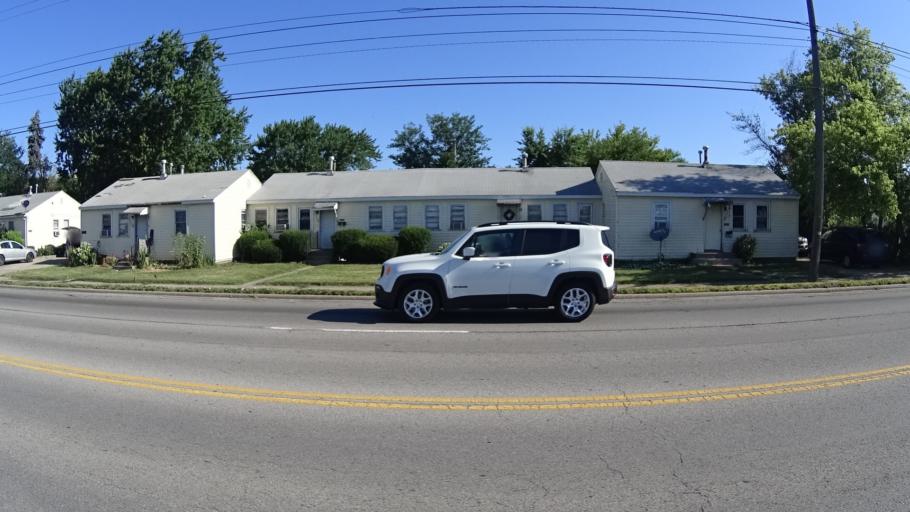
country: US
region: Ohio
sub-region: Erie County
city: Sandusky
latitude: 41.4333
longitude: -82.7233
